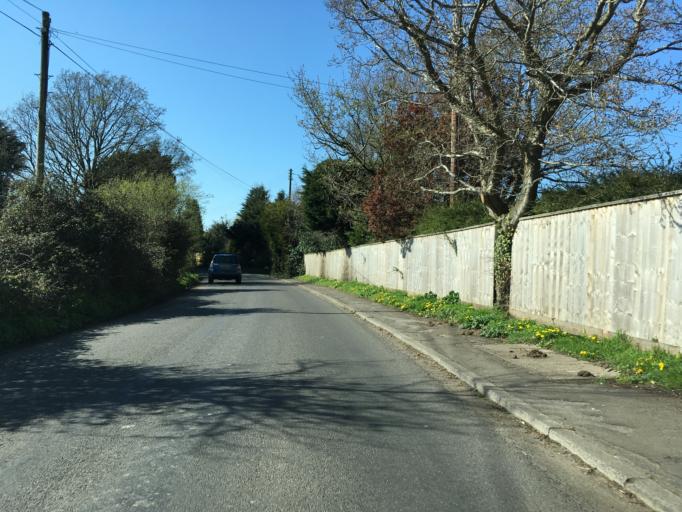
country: GB
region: England
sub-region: North Somerset
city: Easton-in-Gordano
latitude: 51.4805
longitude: -2.7296
